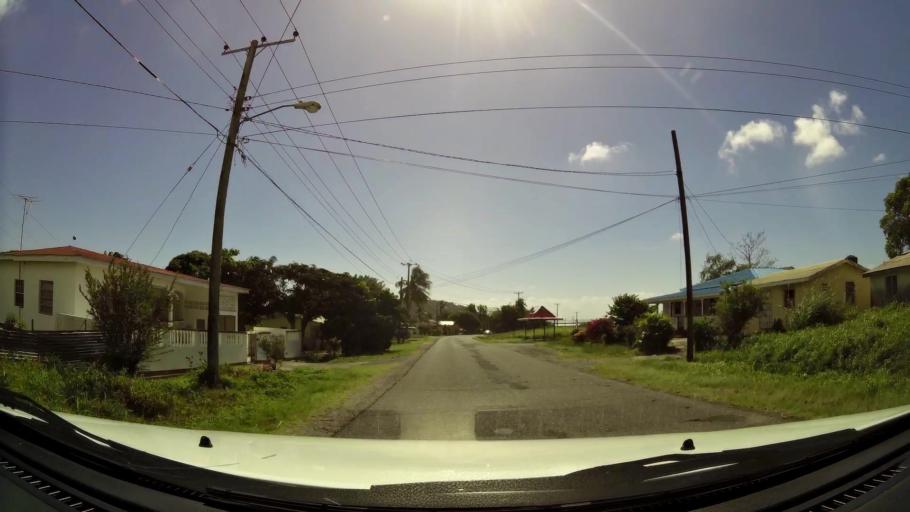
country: LC
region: Laborie Quarter
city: Laborie
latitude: 13.7565
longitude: -60.9723
